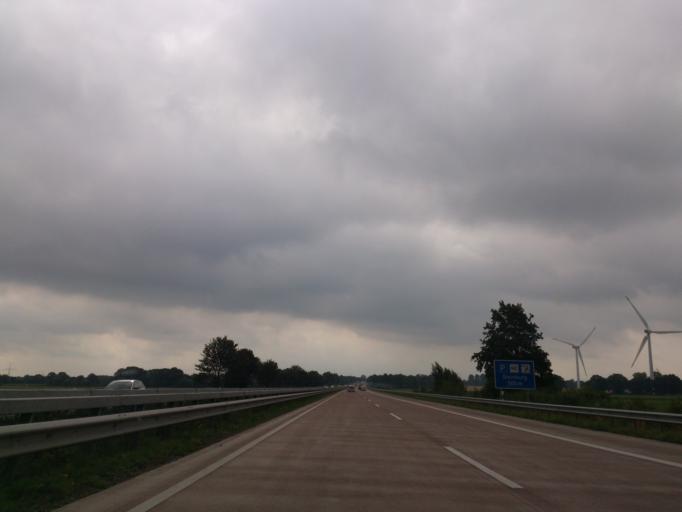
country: DE
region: Schleswig-Holstein
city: Hohenfelde
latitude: 53.8346
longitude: 9.6203
